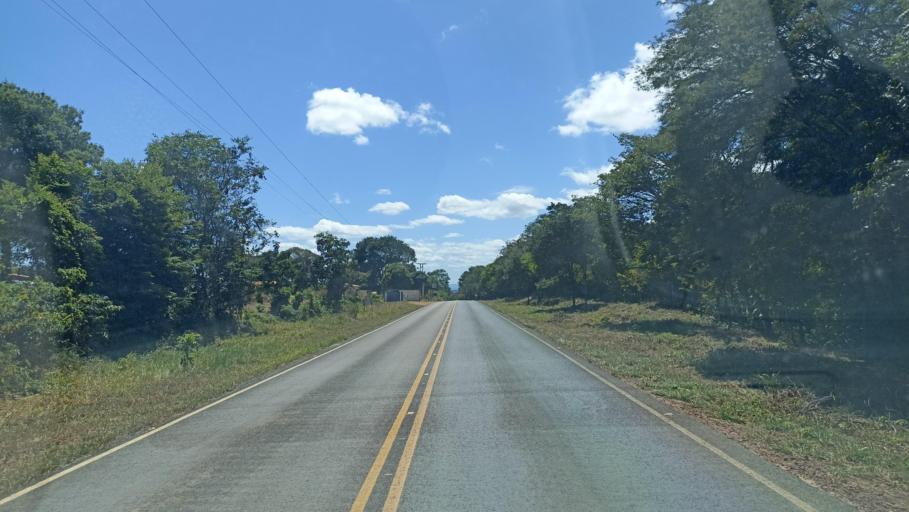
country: BR
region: Bahia
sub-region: Andarai
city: Vera Cruz
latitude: -12.7899
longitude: -41.3286
